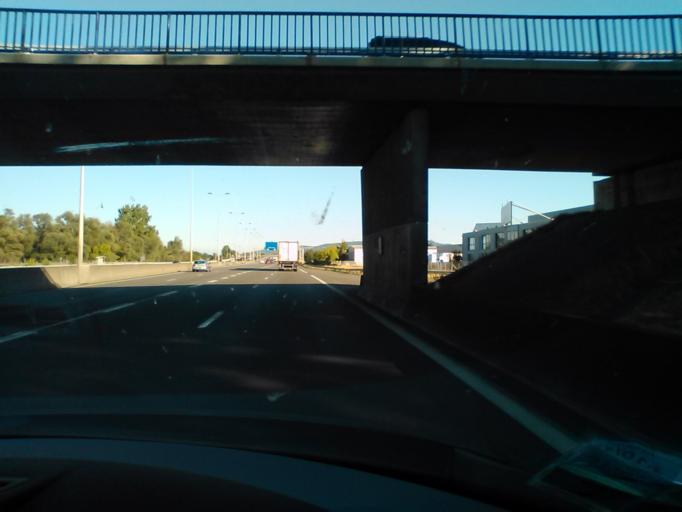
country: FR
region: Rhone-Alpes
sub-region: Departement du Rhone
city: Anse
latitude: 45.9423
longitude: 4.7200
